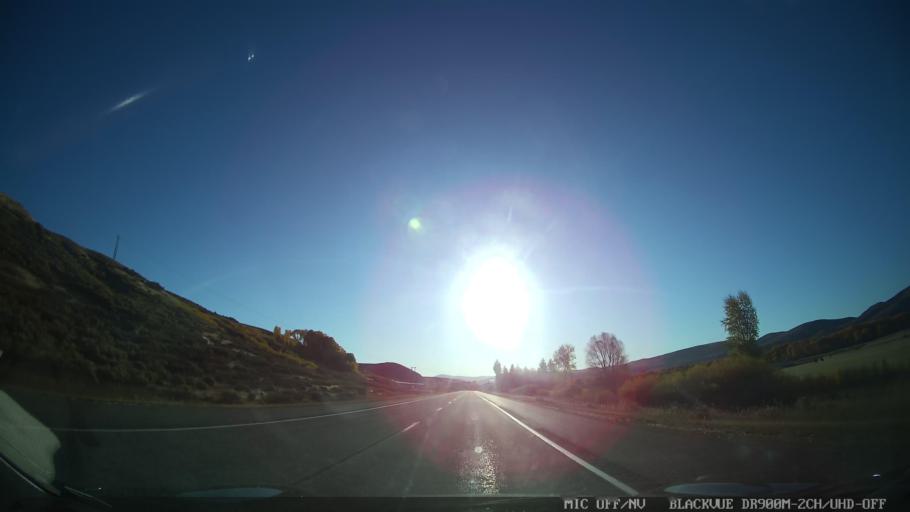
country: US
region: Colorado
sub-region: Grand County
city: Kremmling
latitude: 40.0675
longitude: -106.2650
